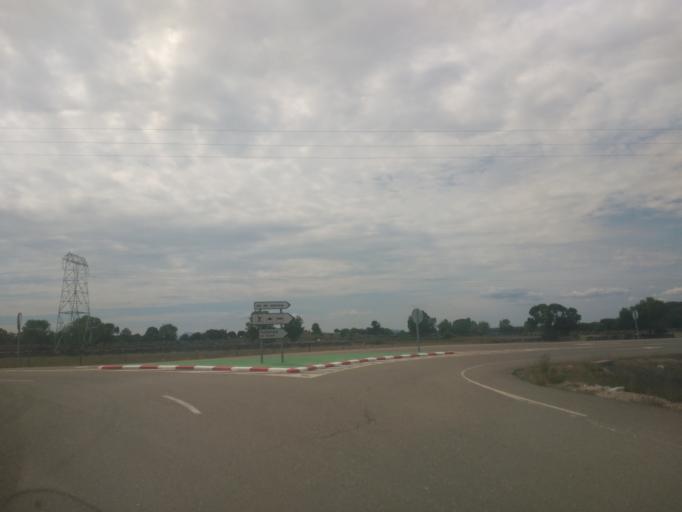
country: ES
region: Castille and Leon
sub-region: Provincia de Salamanca
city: Nava de Bejar
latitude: 40.4820
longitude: -5.6787
